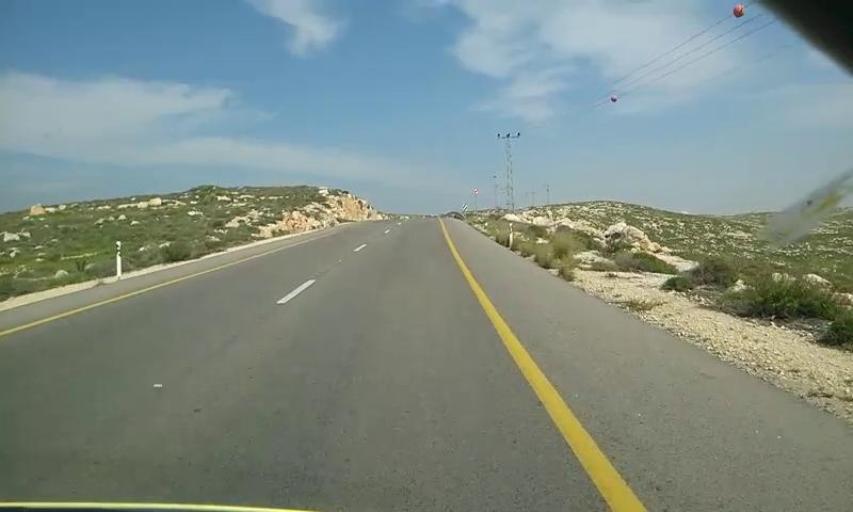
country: PS
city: Rabud
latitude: 31.3937
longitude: 35.0196
